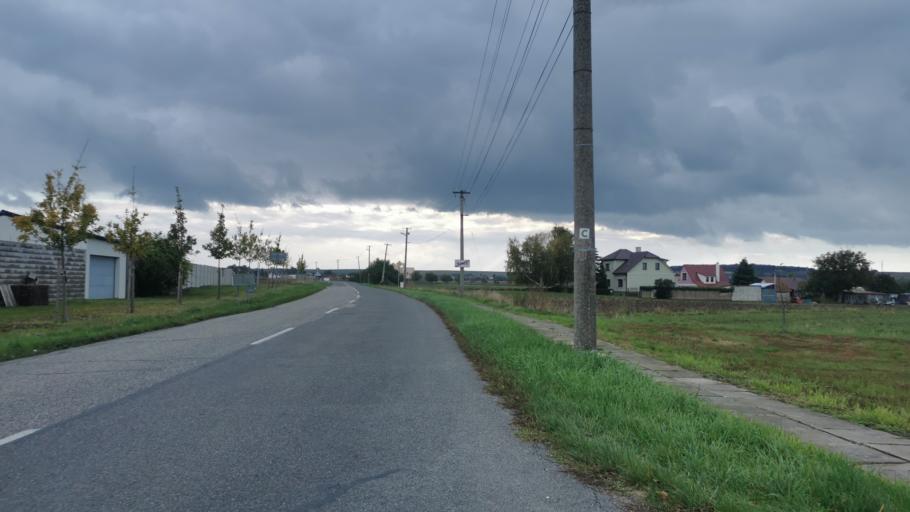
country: SK
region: Trnavsky
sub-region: Okres Skalica
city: Holic
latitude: 48.8180
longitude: 17.1940
